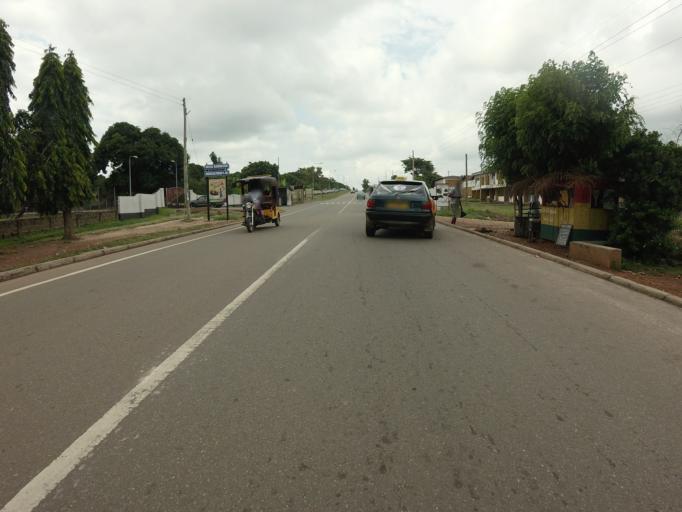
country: GH
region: Volta
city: Ho
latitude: 6.6129
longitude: 0.4870
